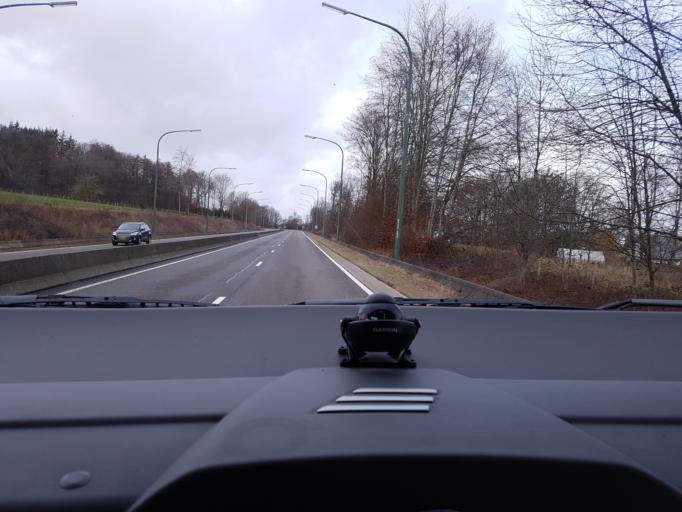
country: BE
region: Wallonia
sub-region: Province du Luxembourg
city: Marche-en-Famenne
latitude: 50.2075
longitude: 5.3671
